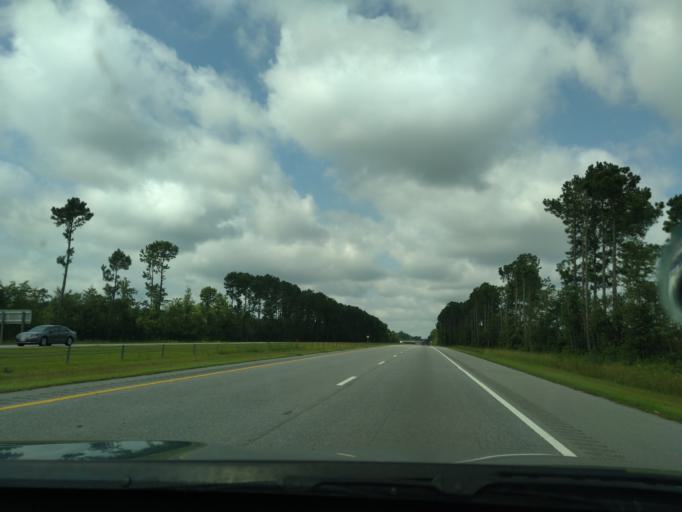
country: US
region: North Carolina
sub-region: Martin County
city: Williamston
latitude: 35.8274
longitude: -77.1420
